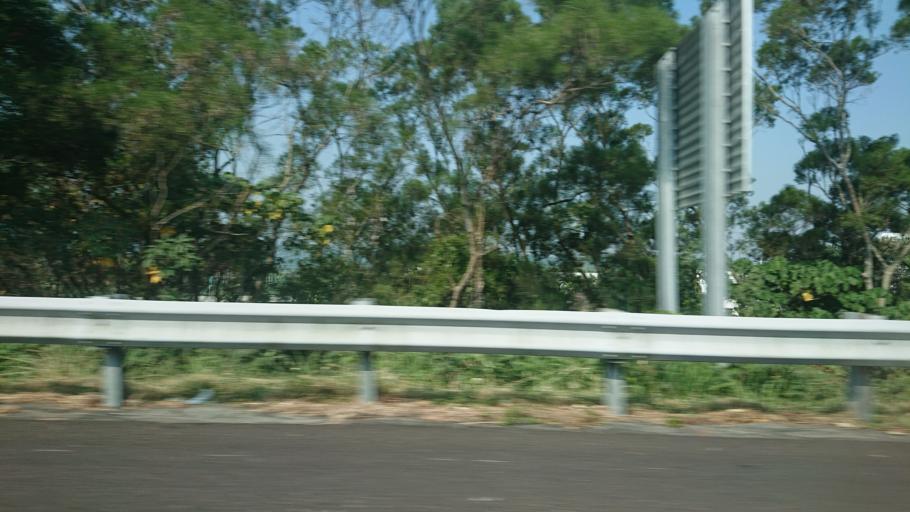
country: TW
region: Taiwan
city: Lugu
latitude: 23.8221
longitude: 120.7063
